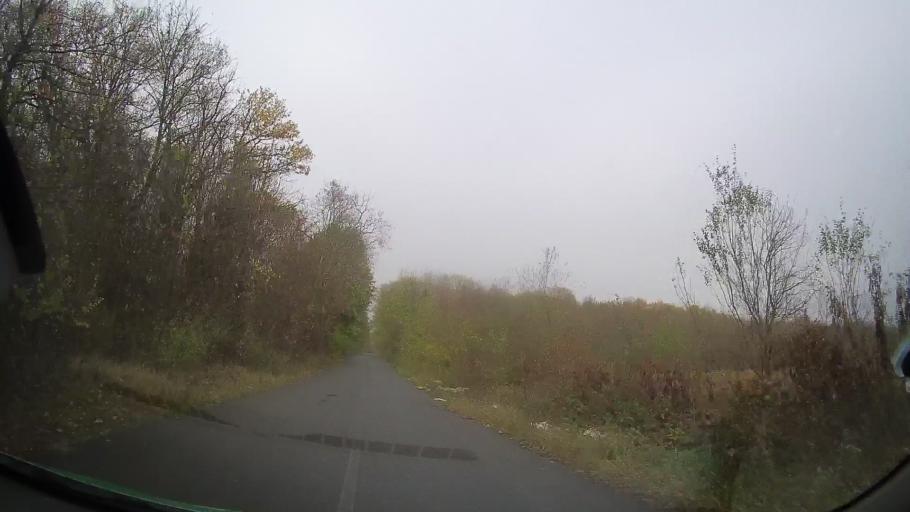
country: RO
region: Prahova
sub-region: Comuna Balta Doamnei
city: Balta Doamnei
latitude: 44.7562
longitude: 26.1296
